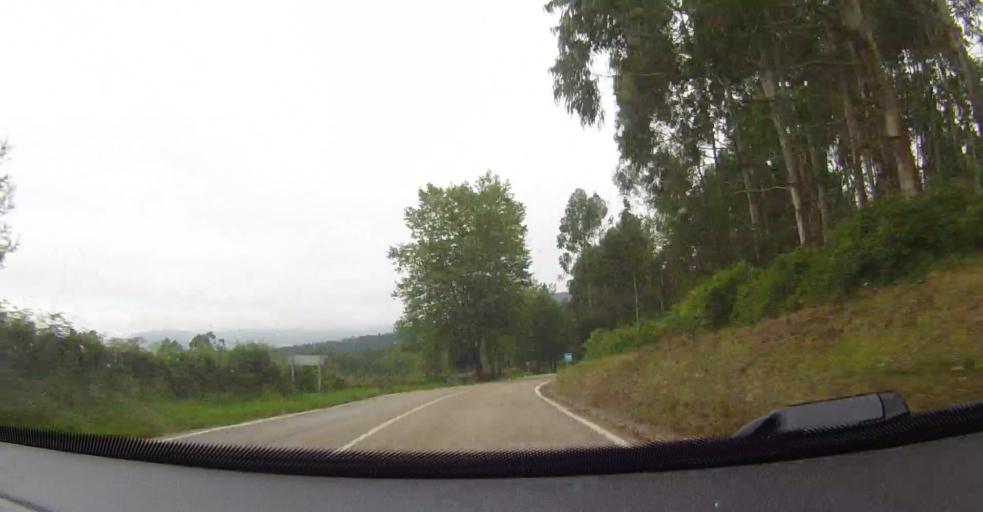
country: ES
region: Basque Country
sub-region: Bizkaia
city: Balmaseda
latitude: 43.2375
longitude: -3.2934
